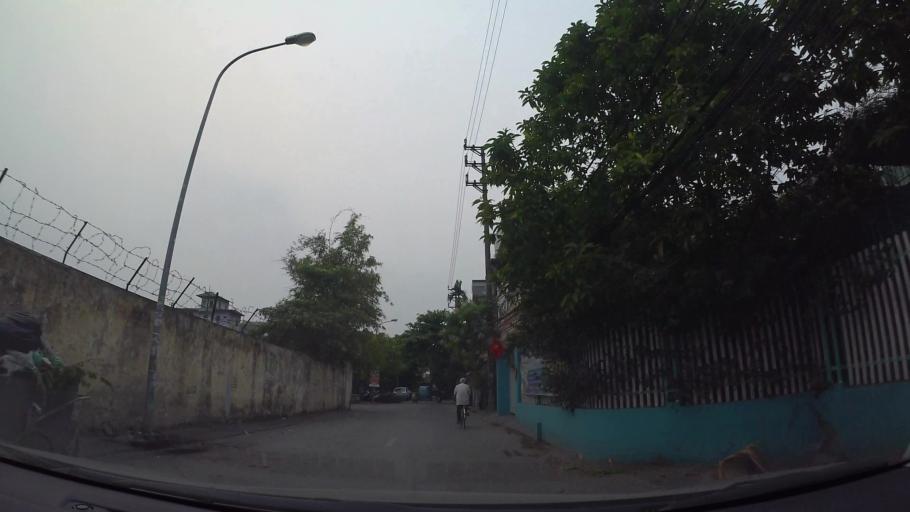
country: VN
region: Ha Noi
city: Hoan Kiem
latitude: 21.0583
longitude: 105.8948
